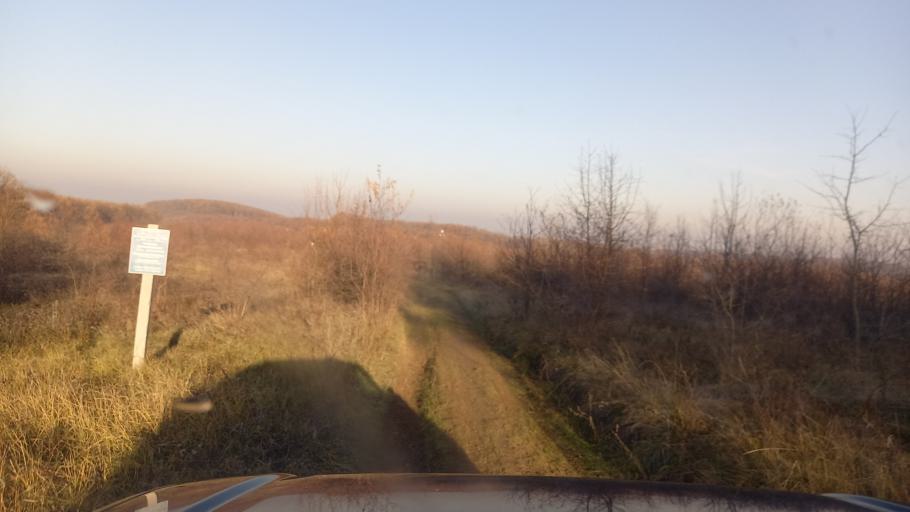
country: RU
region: Krasnodarskiy
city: Azovskaya
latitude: 44.8068
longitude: 38.5919
